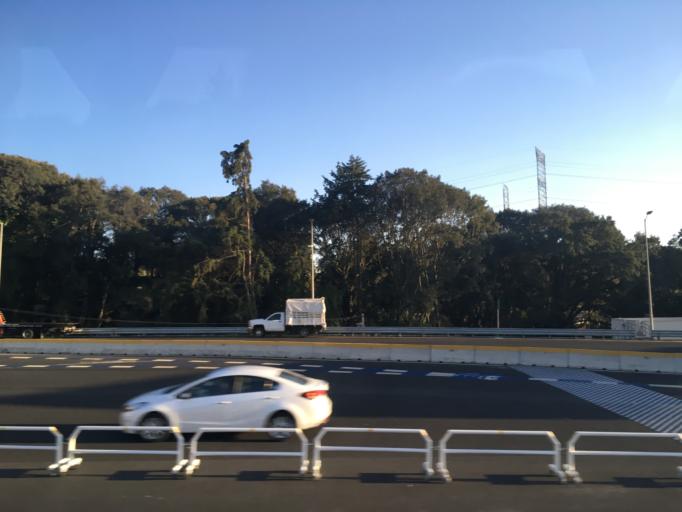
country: MX
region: Mexico
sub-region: Lerma
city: San Miguel Ameyalco
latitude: 19.2904
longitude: -99.4349
